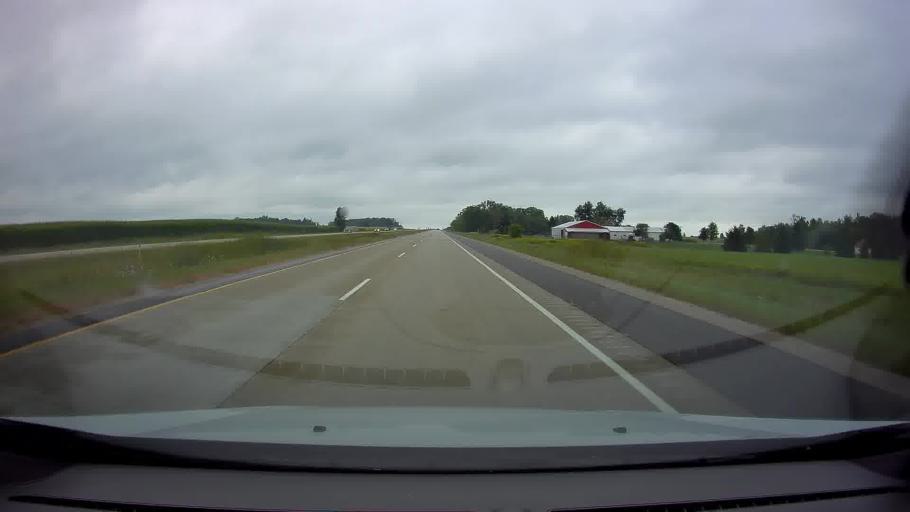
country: US
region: Wisconsin
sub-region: Brown County
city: Pulaski
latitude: 44.6378
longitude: -88.2857
